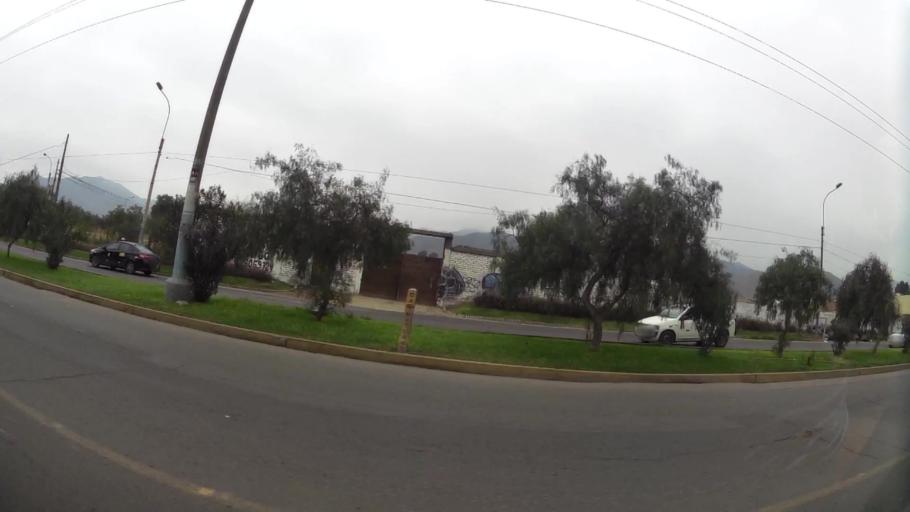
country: PE
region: Lima
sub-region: Lima
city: La Molina
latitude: -12.0860
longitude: -76.8996
